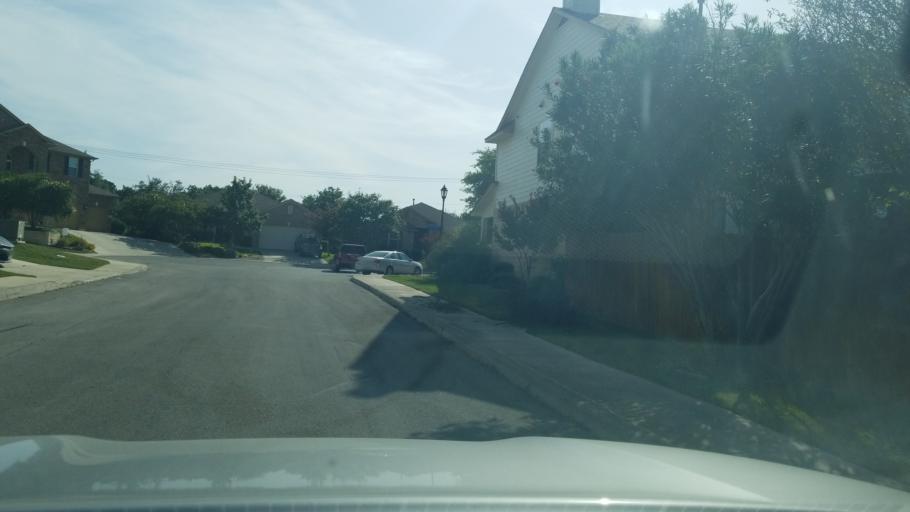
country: US
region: Texas
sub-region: Bexar County
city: Timberwood Park
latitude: 29.6874
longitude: -98.4783
